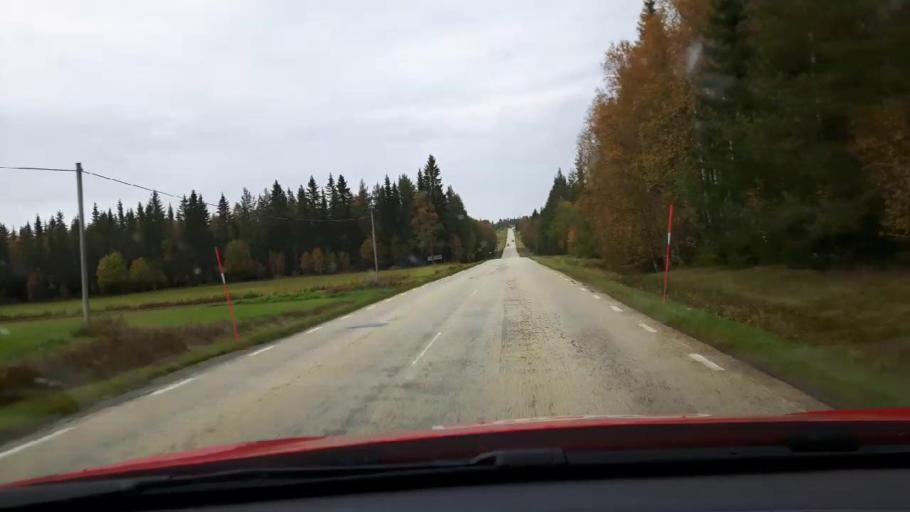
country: SE
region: Jaemtland
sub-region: Bergs Kommun
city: Hoverberg
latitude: 62.9285
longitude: 14.3352
